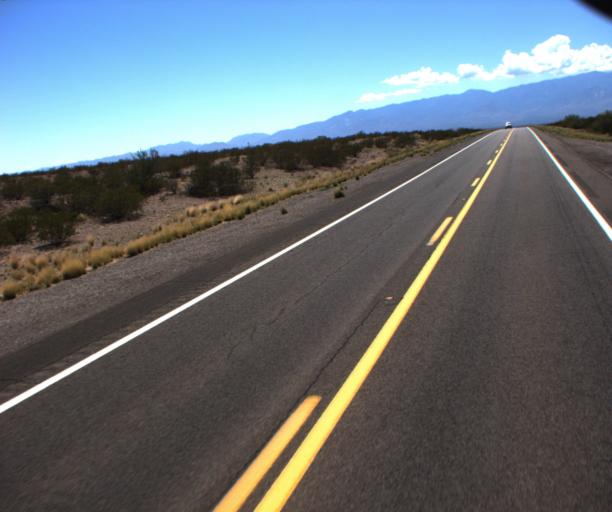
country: US
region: Arizona
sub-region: Graham County
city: Safford
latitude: 32.7981
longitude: -109.5341
